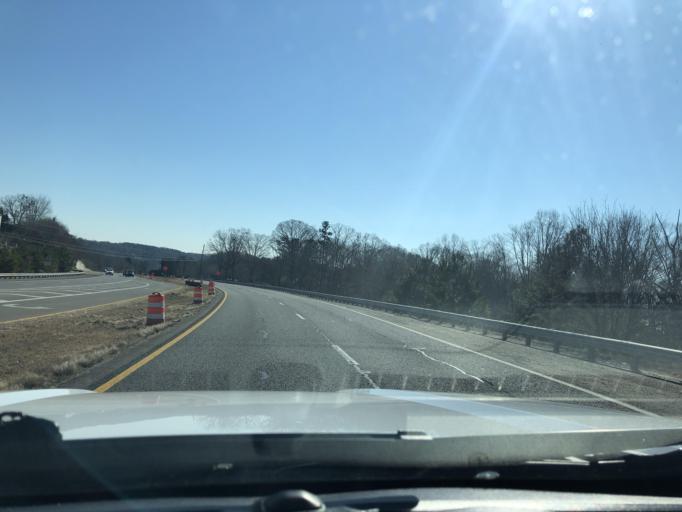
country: US
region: Georgia
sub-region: Hall County
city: Gainesville
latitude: 34.3270
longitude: -83.8888
